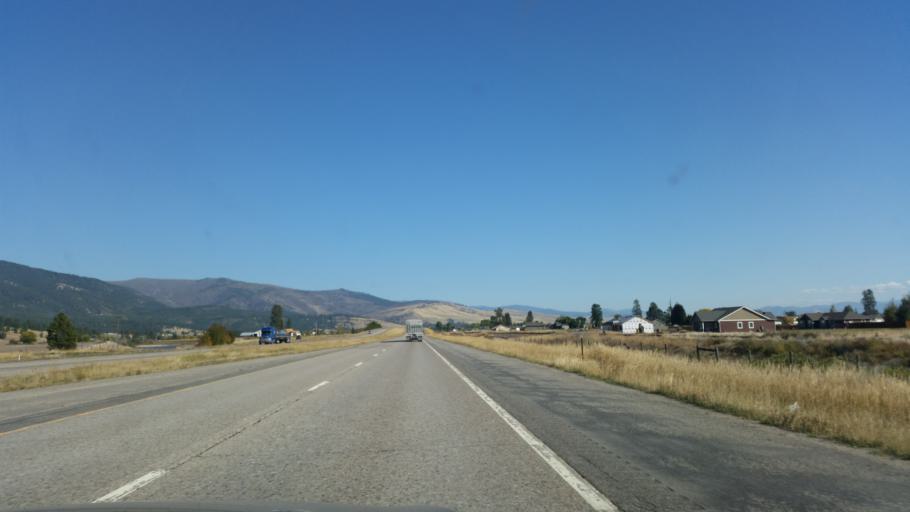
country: US
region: Montana
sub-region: Missoula County
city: Frenchtown
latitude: 47.0286
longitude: -114.3036
